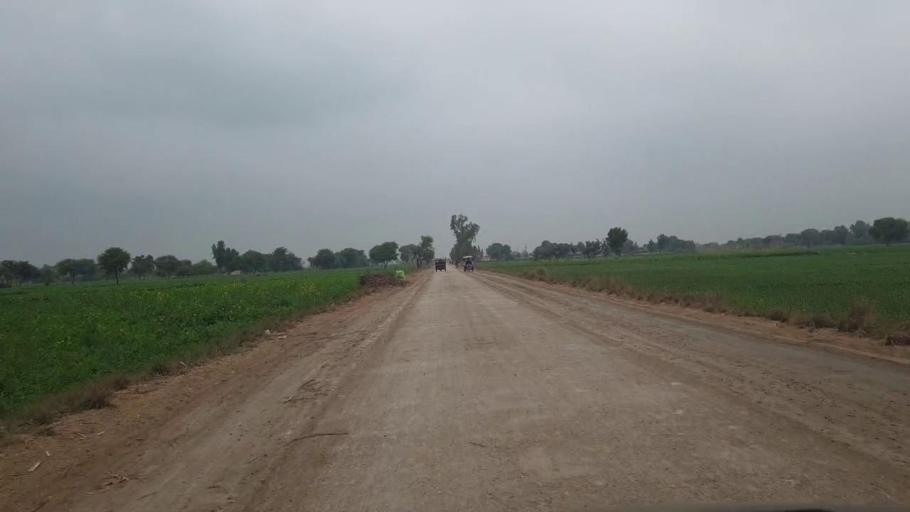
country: PK
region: Sindh
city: Shahdadpur
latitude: 25.9417
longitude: 68.7252
